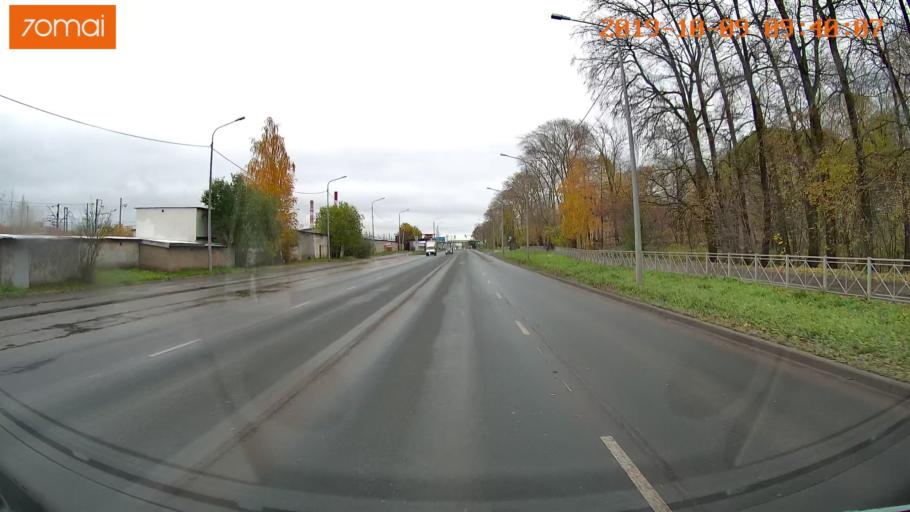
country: RU
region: Vologda
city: Vologda
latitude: 59.1964
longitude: 39.9210
